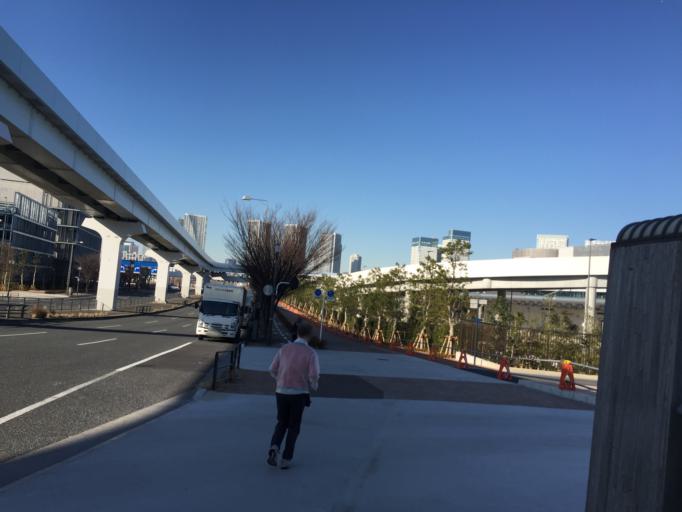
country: JP
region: Tokyo
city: Tokyo
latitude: 35.6431
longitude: 139.7865
